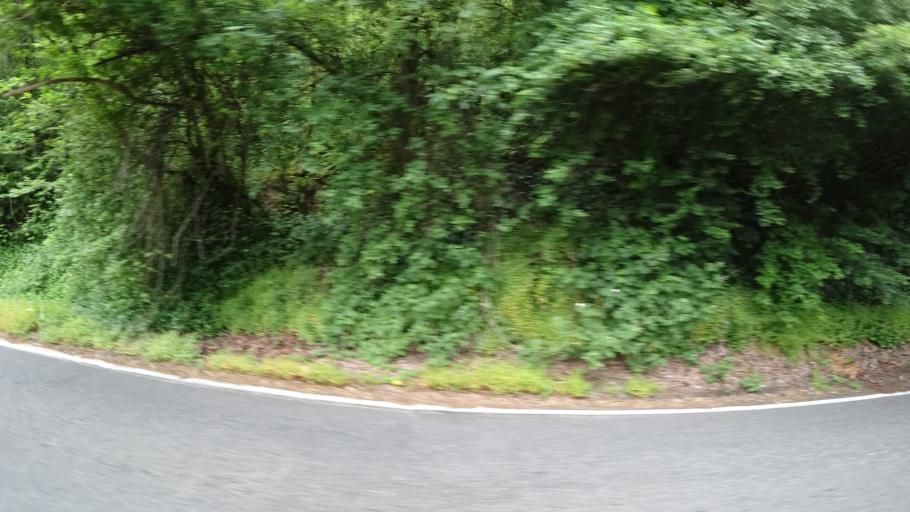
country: US
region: Oregon
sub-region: Multnomah County
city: Portland
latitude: 45.5044
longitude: -122.6919
